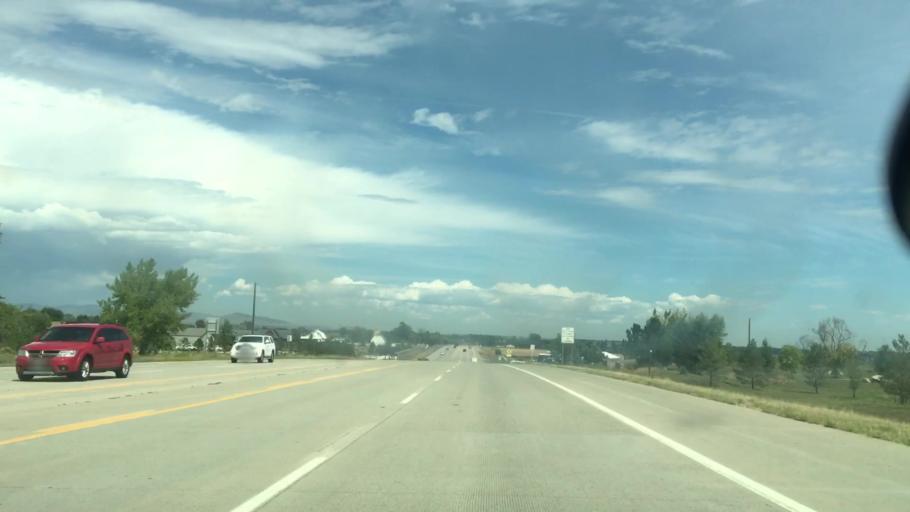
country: US
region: Colorado
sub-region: Larimer County
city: Berthoud
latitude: 40.2593
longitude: -105.1025
